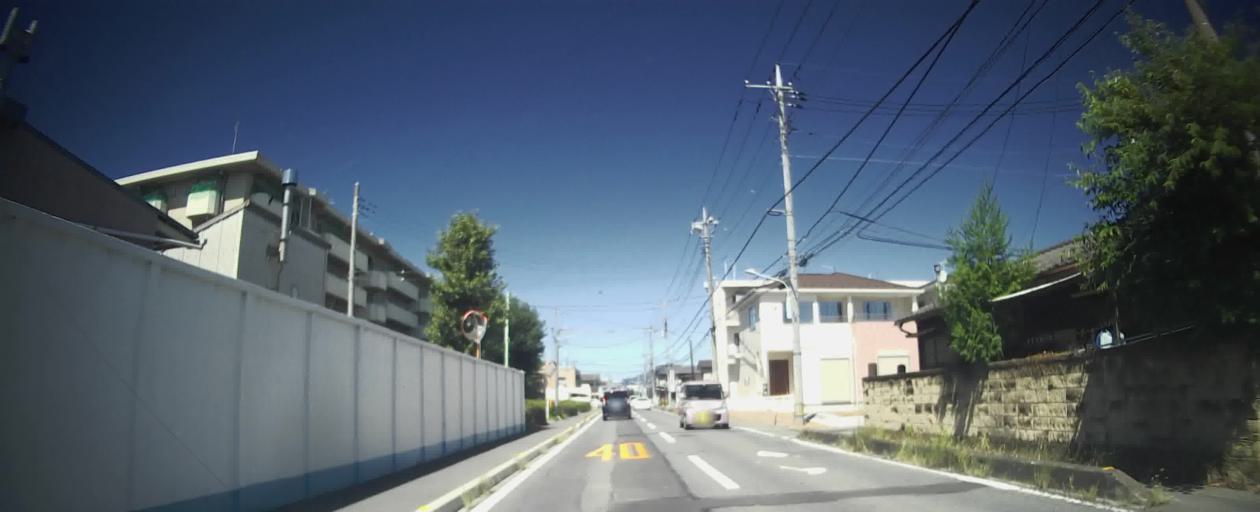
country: JP
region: Gunma
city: Maebashi-shi
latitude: 36.4030
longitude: 139.0549
